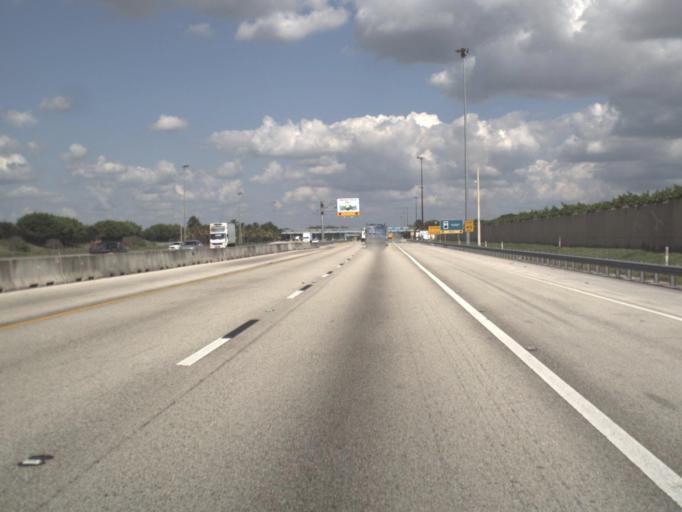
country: US
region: Florida
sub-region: Palm Beach County
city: Seminole Manor
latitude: 26.5572
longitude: -80.1729
